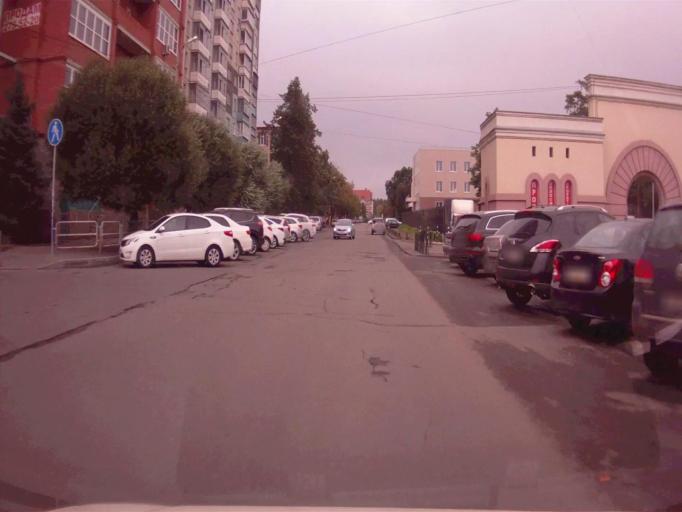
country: RU
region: Chelyabinsk
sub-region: Gorod Chelyabinsk
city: Chelyabinsk
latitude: 55.1620
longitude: 61.3683
